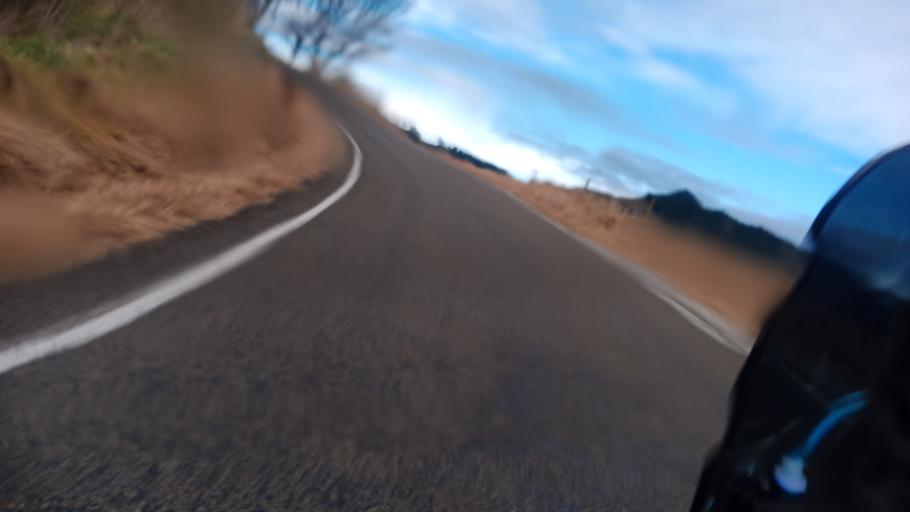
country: NZ
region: Gisborne
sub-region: Gisborne District
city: Gisborne
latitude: -38.4035
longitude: 177.9538
